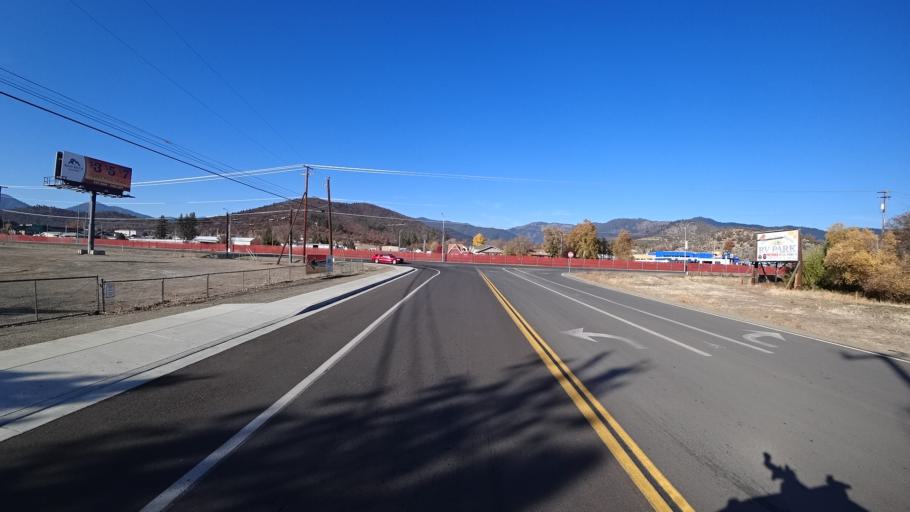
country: US
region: California
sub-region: Siskiyou County
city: Yreka
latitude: 41.7093
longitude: -122.6410
